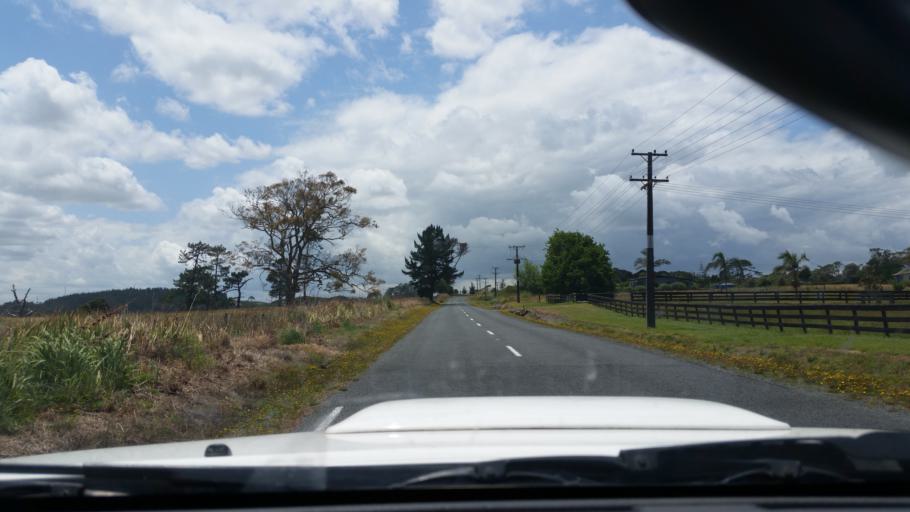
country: NZ
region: Northland
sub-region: Kaipara District
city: Dargaville
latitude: -35.9177
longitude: 173.8216
